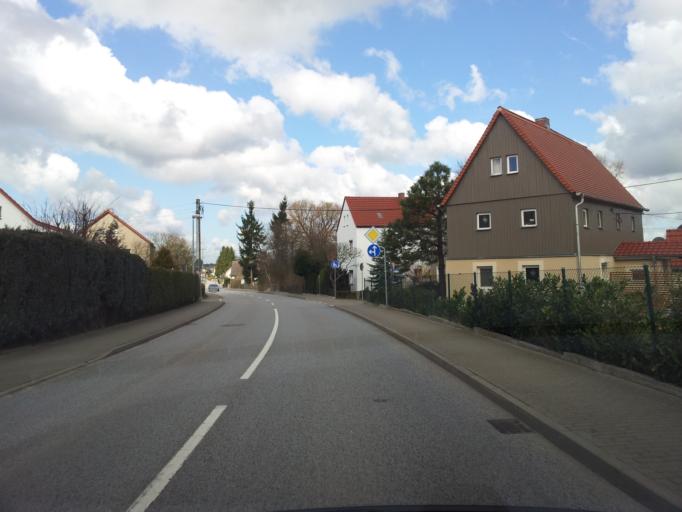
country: DE
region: Saxony
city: Ottendorf-Okrilla
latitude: 51.1830
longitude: 13.8460
